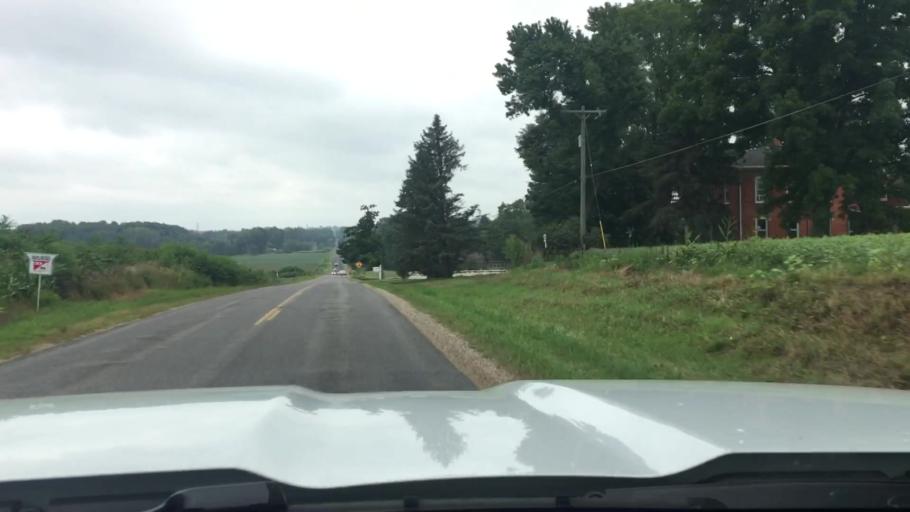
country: US
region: Michigan
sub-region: Ottawa County
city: Hudsonville
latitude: 42.7857
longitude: -85.8616
